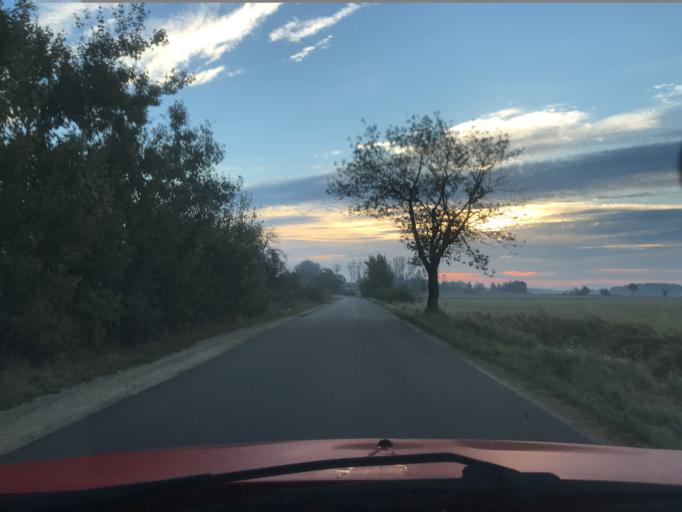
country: PL
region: Greater Poland Voivodeship
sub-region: Powiat ostrowski
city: Raszkow
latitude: 51.7183
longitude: 17.7590
